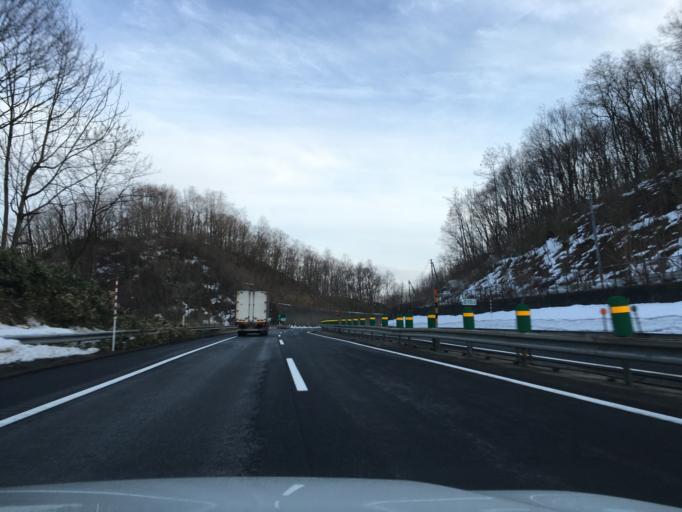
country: JP
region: Akita
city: Hanawa
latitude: 40.3604
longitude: 140.7281
